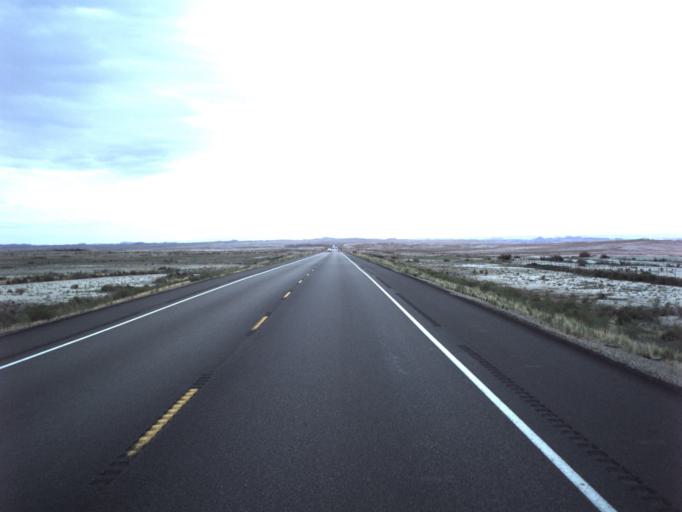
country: US
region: Utah
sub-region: Carbon County
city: East Carbon City
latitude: 39.0008
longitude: -110.2685
